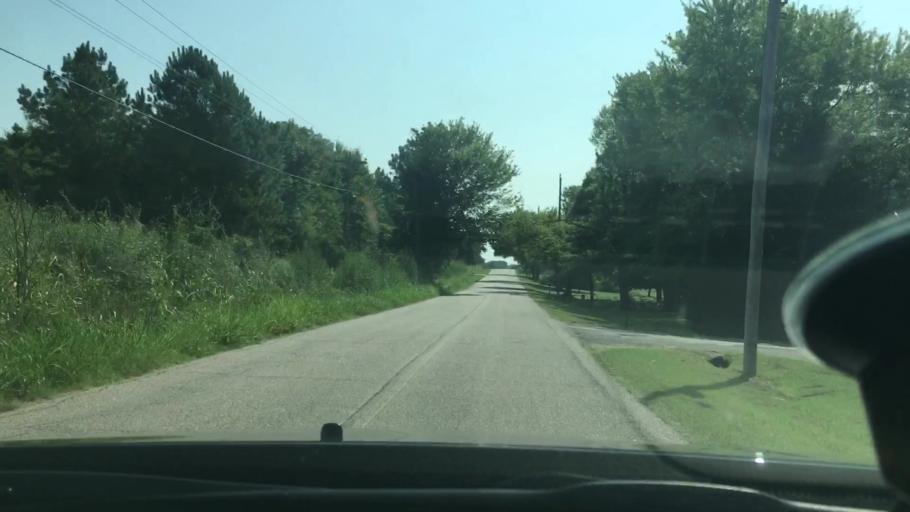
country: US
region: Oklahoma
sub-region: Bryan County
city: Durant
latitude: 34.0121
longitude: -96.4318
